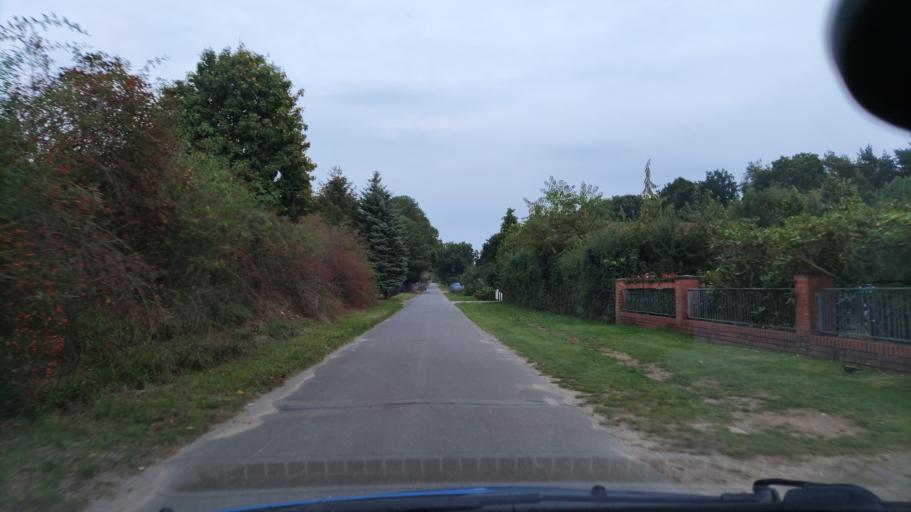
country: DE
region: Lower Saxony
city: Karwitz
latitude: 53.0903
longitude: 10.9941
